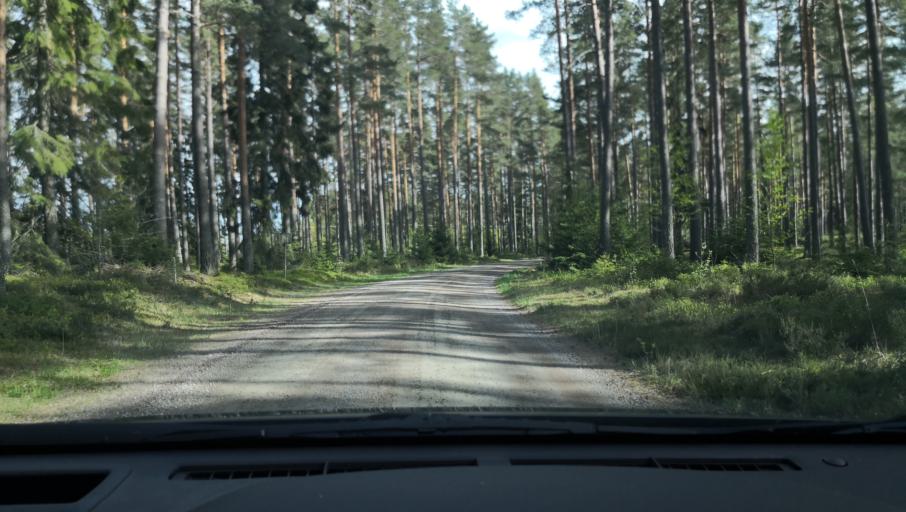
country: SE
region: OErebro
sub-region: Askersunds Kommun
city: Asbro
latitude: 59.0345
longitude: 15.0422
